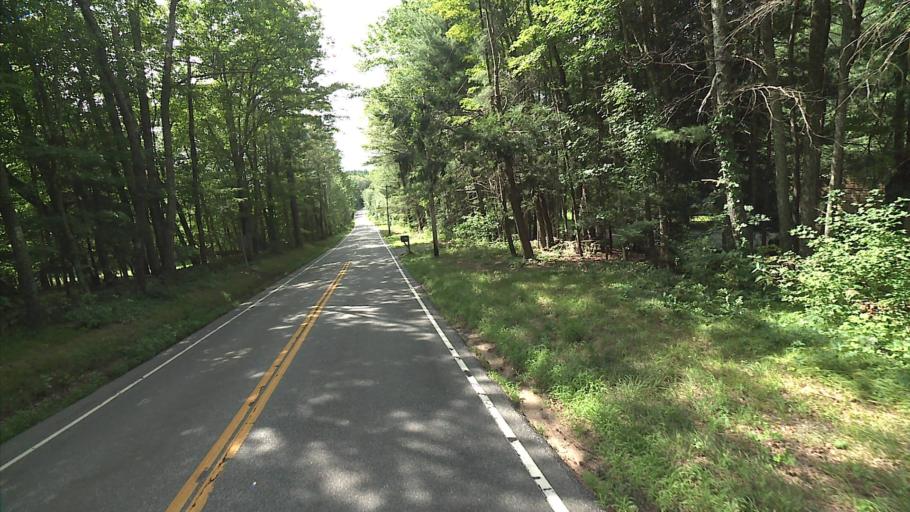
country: US
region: Massachusetts
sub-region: Hampden County
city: Holland
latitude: 41.9740
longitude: -72.1131
